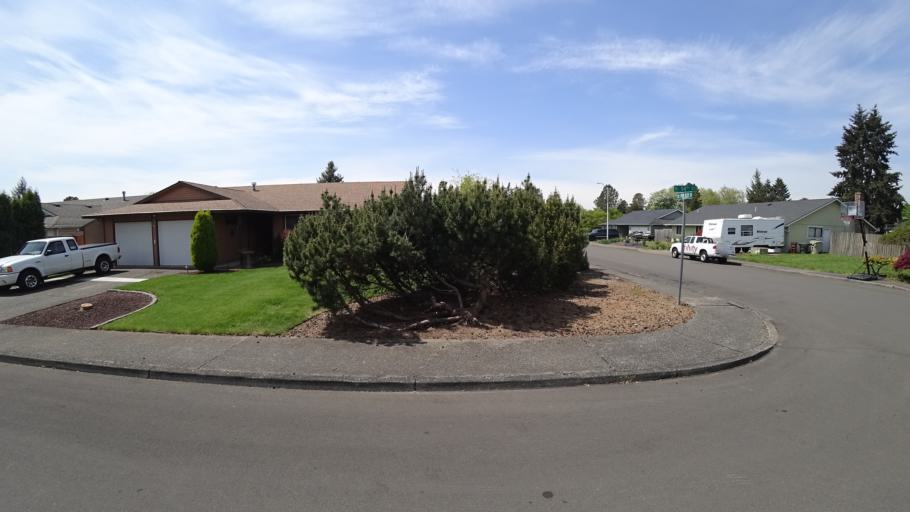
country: US
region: Oregon
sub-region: Washington County
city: Aloha
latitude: 45.5011
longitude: -122.9276
